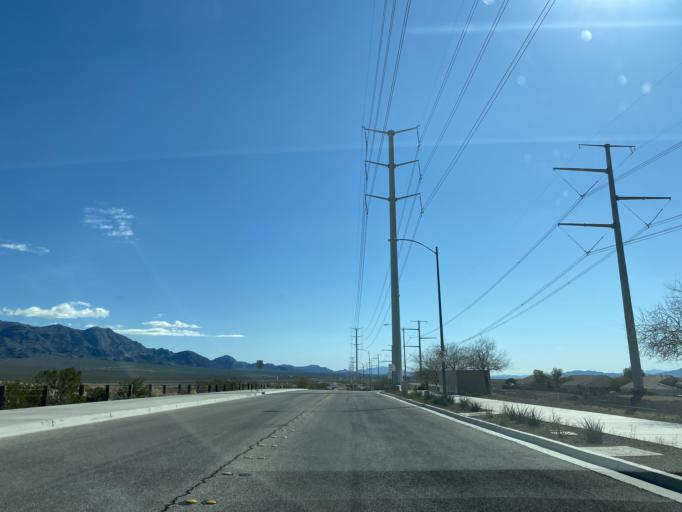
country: US
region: Nevada
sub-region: Clark County
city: North Las Vegas
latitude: 36.3359
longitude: -115.2755
